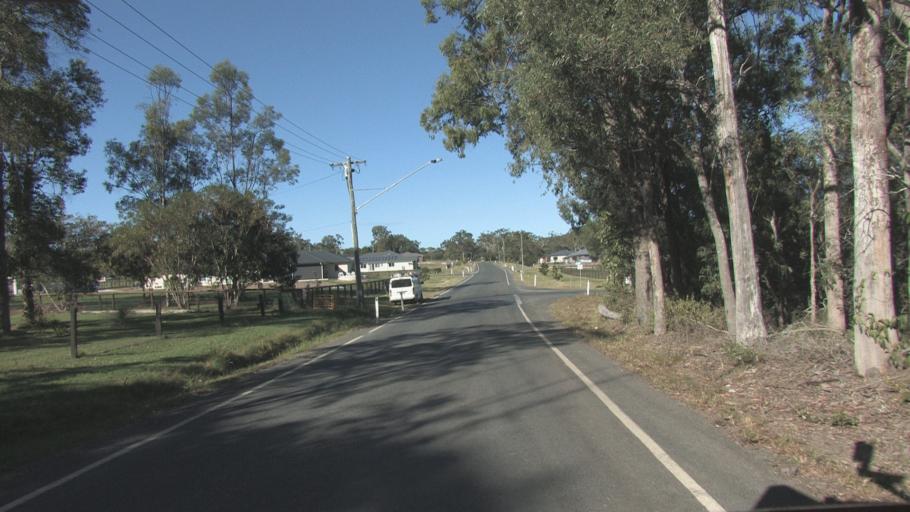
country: AU
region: Queensland
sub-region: Logan
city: Logan Reserve
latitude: -27.7525
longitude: 153.1379
